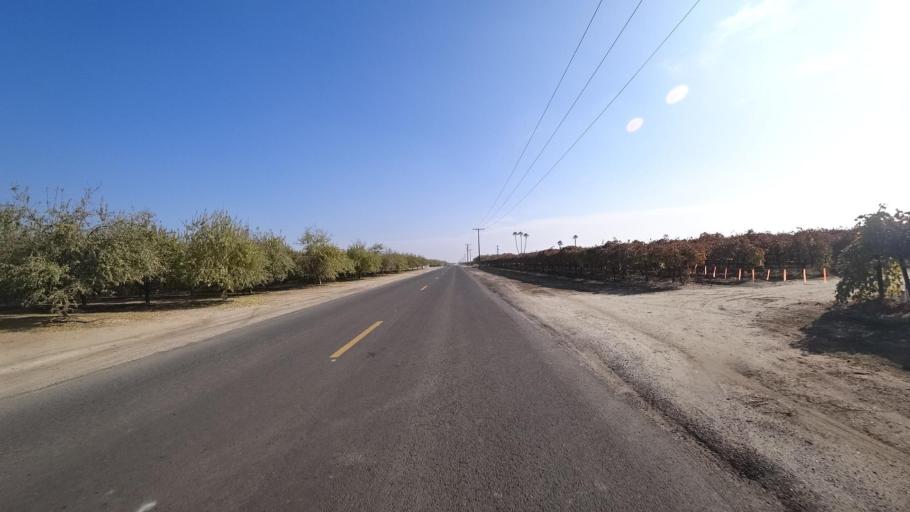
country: US
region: California
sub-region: Kern County
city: McFarland
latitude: 35.6892
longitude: -119.1717
